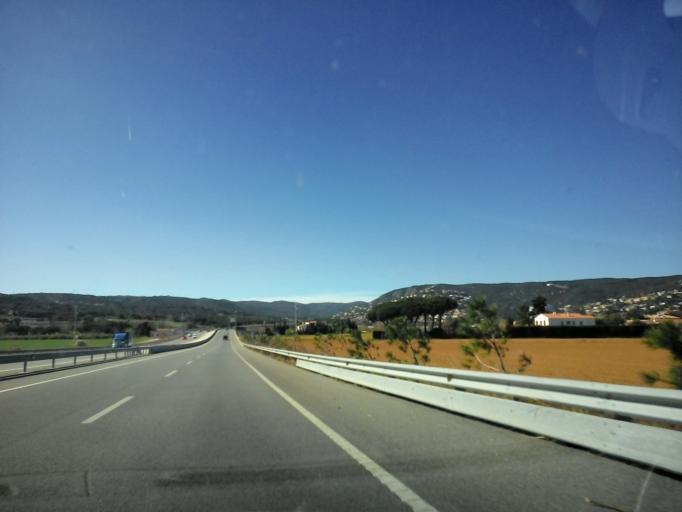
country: ES
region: Catalonia
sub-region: Provincia de Girona
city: Calonge
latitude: 41.8582
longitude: 3.0865
